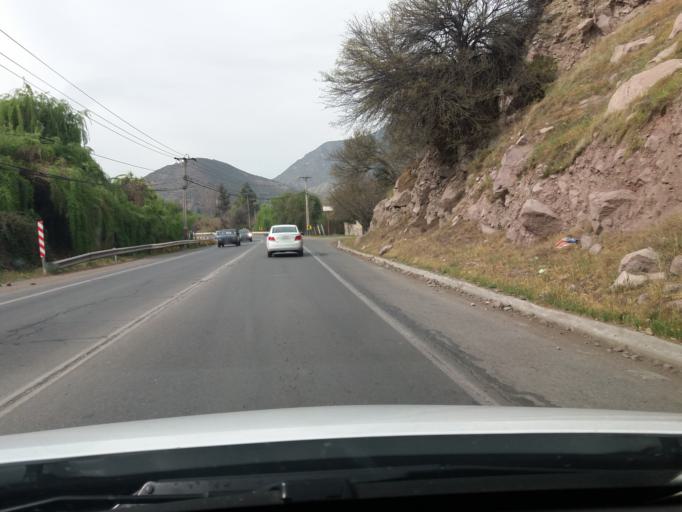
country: CL
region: Valparaiso
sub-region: Provincia de San Felipe
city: San Felipe
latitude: -32.7621
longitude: -70.7354
